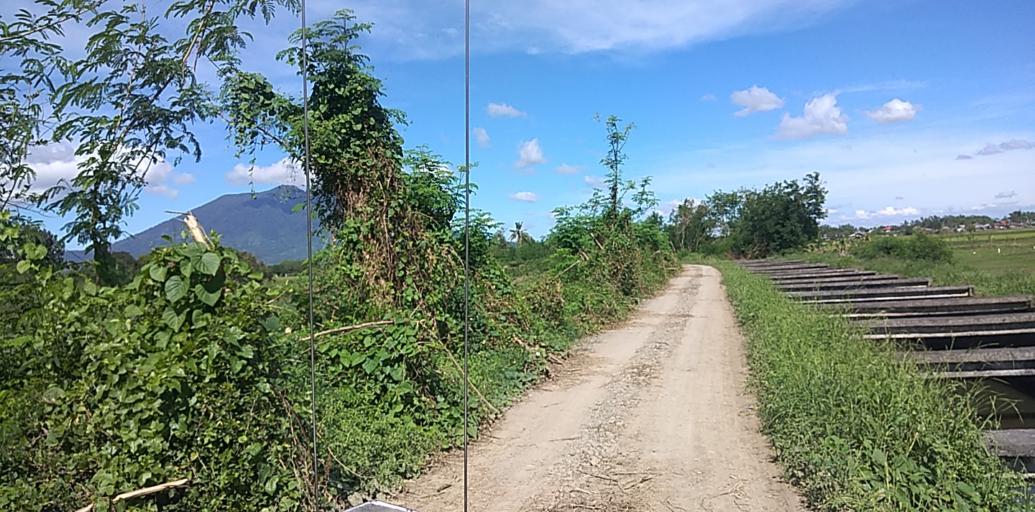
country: PH
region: Central Luzon
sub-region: Province of Pampanga
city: Candating
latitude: 15.1282
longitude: 120.7983
